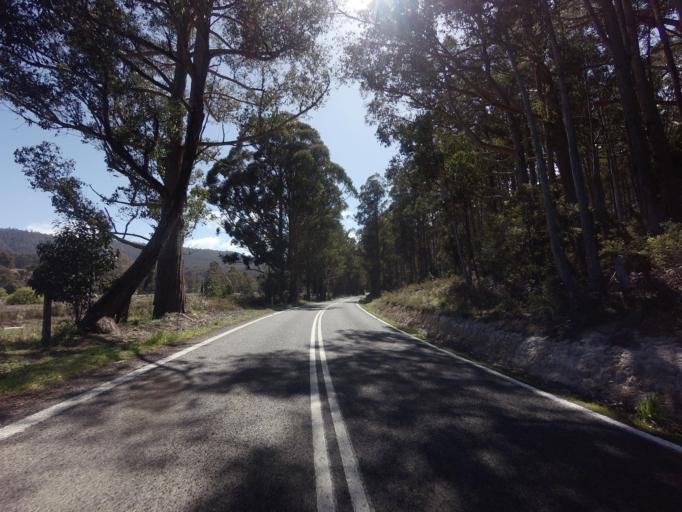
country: AU
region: Tasmania
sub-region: Derwent Valley
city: New Norfolk
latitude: -42.6972
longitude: 146.7130
